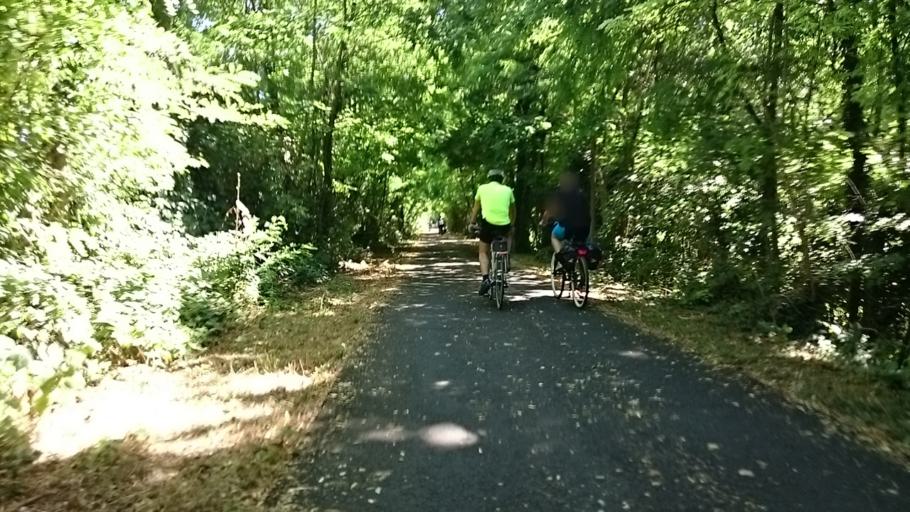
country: IT
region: Veneto
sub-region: Provincia di Padova
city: Torreselle
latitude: 45.6090
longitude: 12.0260
